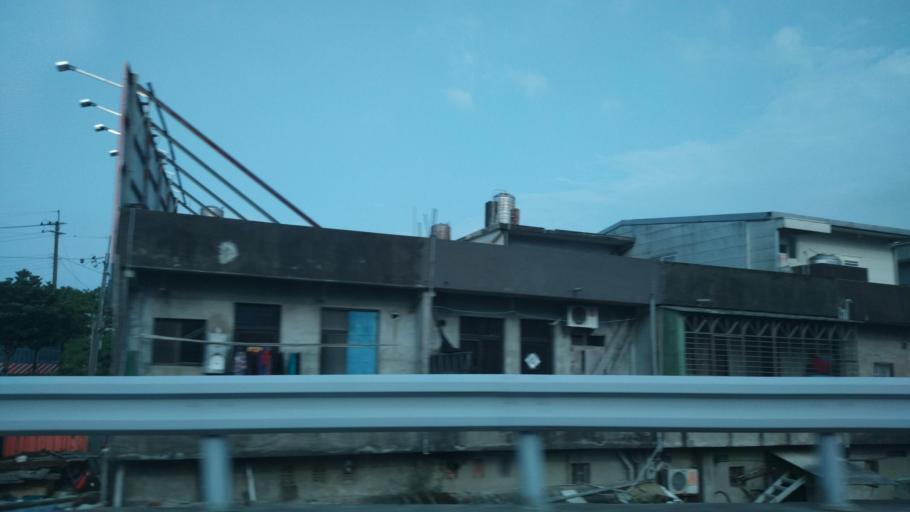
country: TW
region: Taiwan
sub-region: Keelung
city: Keelung
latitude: 25.2277
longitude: 121.6296
